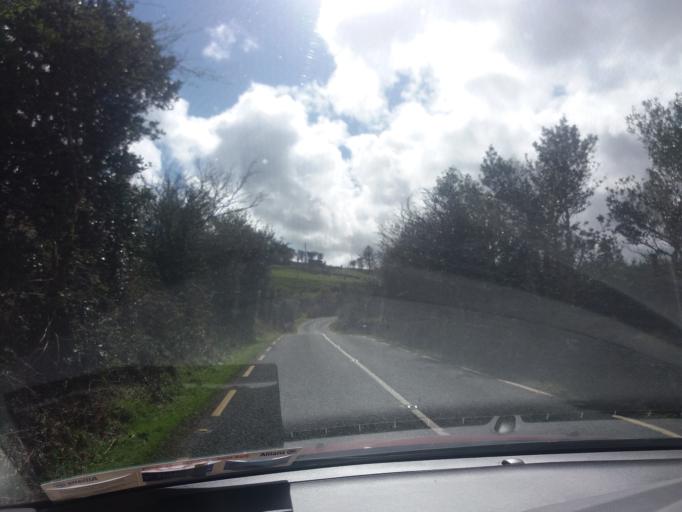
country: IE
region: Munster
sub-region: Ciarrai
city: Dingle
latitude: 52.2120
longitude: -10.1629
